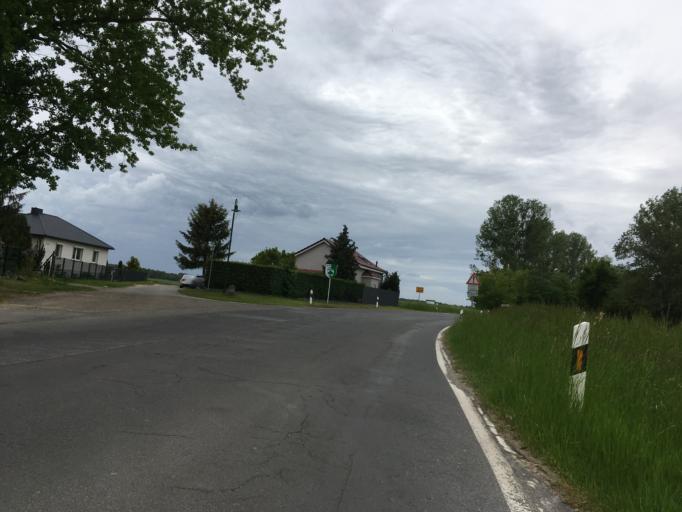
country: DE
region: Brandenburg
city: Werneuchen
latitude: 52.6634
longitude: 13.6763
